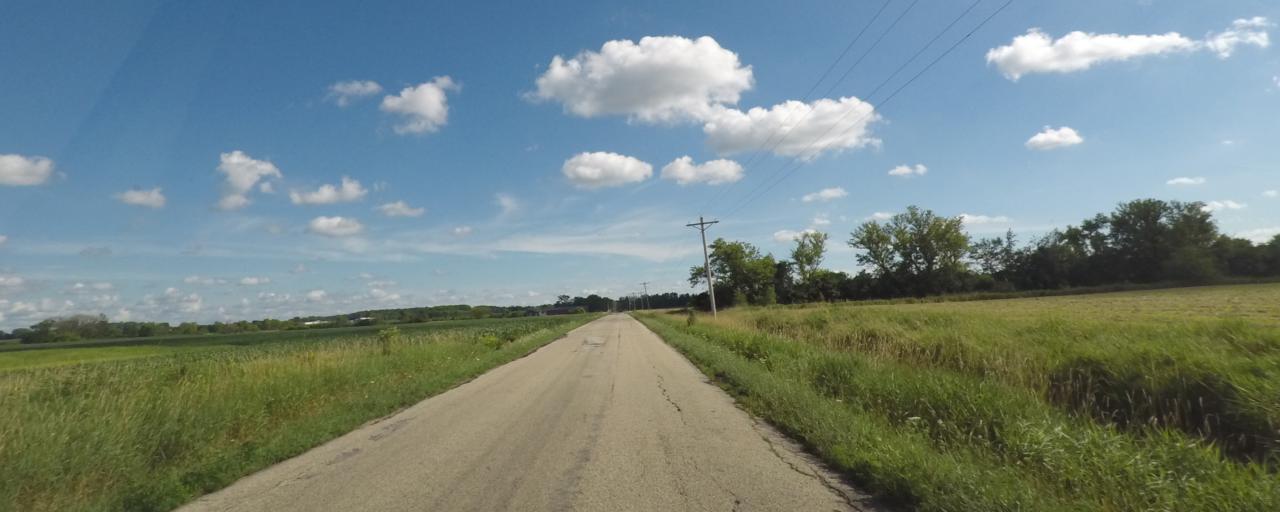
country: US
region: Wisconsin
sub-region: Rock County
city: Edgerton
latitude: 42.8443
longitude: -89.1320
